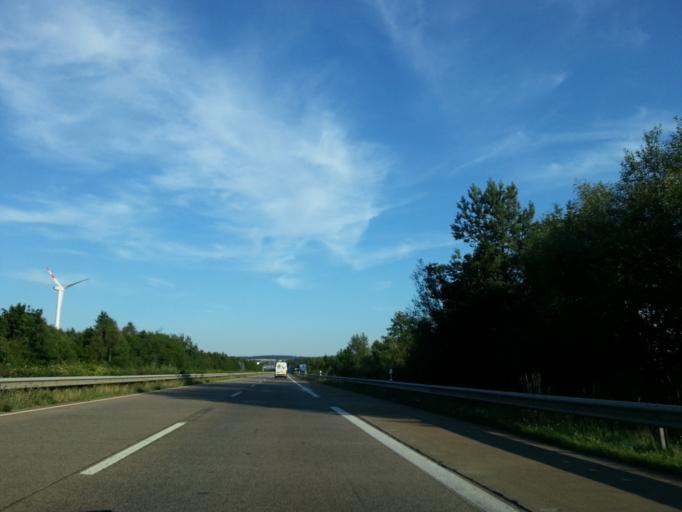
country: DE
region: Rheinland-Pfalz
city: Hinzert-Polert
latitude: 49.6857
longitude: 6.9039
